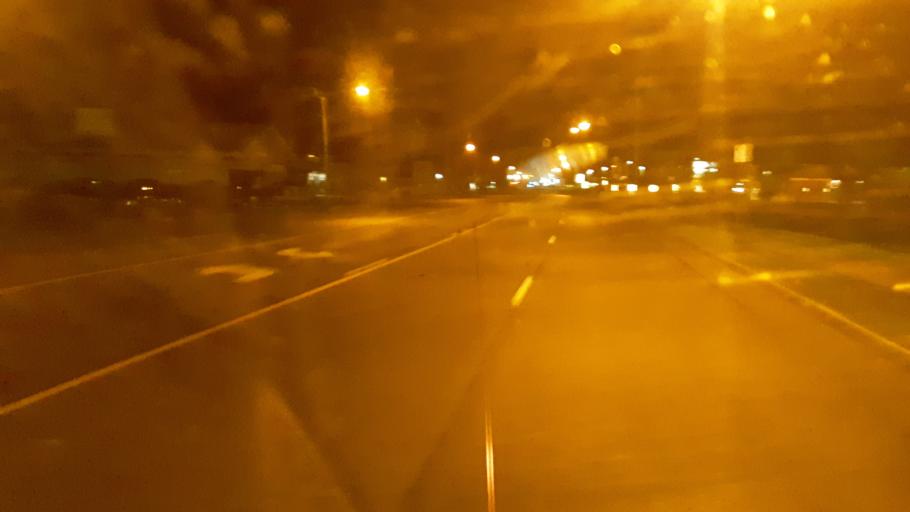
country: US
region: New York
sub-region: Oneida County
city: Rome
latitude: 43.2240
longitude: -75.4847
